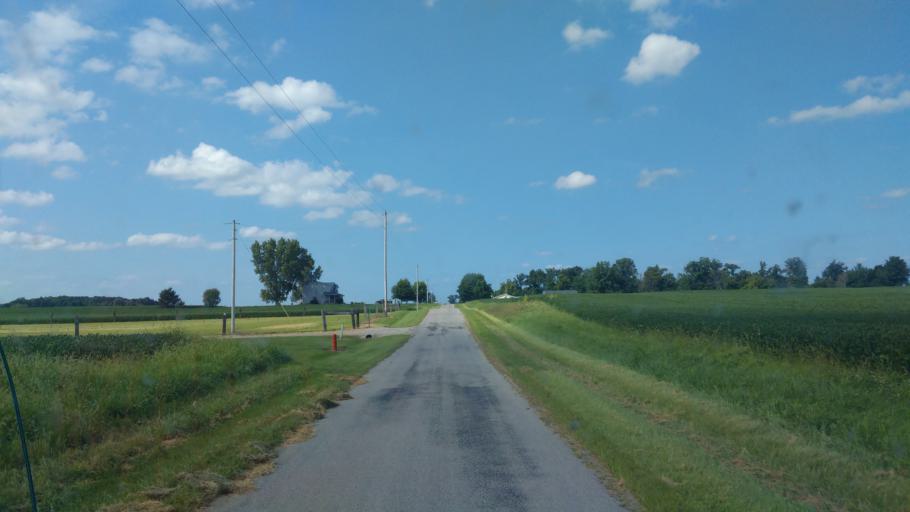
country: US
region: Ohio
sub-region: Union County
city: Richwood
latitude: 40.5082
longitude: -83.4510
